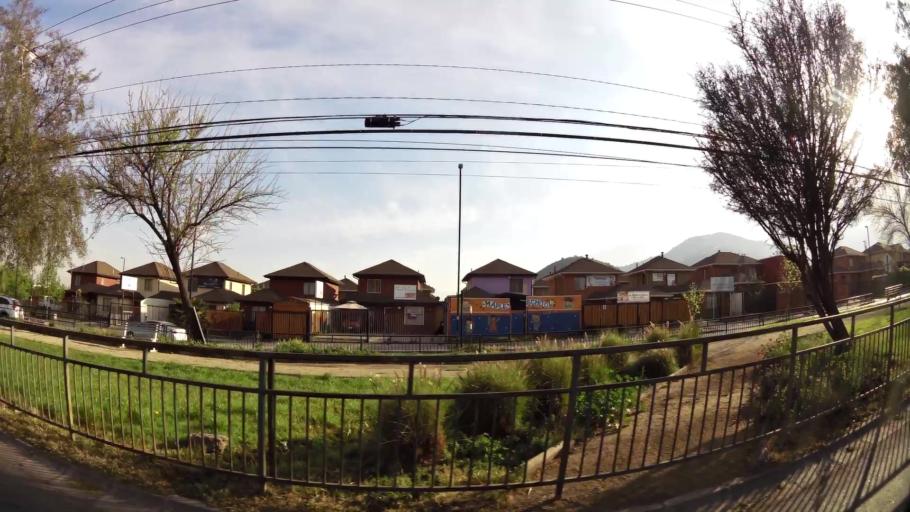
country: CL
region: Santiago Metropolitan
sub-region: Provincia de Cordillera
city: Puente Alto
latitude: -33.5594
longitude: -70.5518
